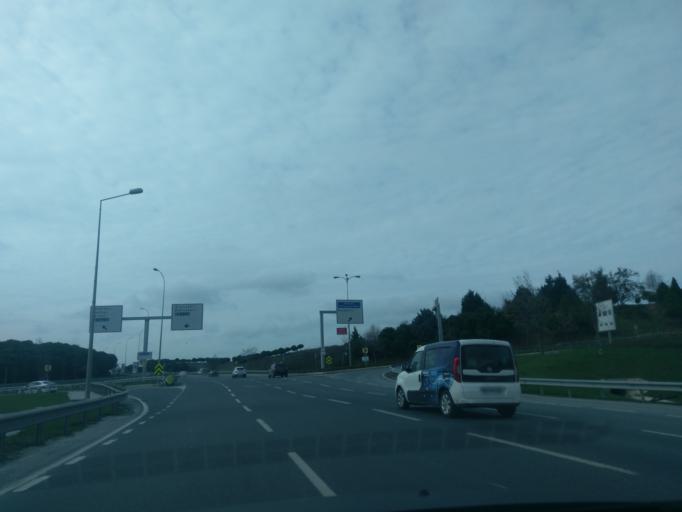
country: TR
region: Istanbul
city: Basaksehir
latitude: 41.0632
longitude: 28.7660
